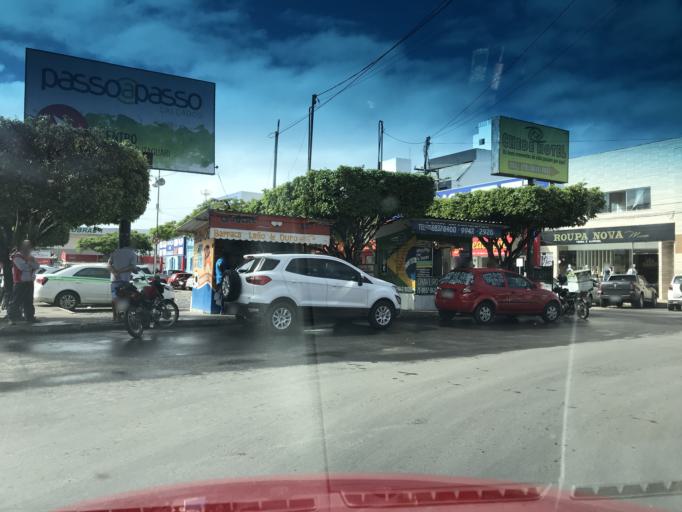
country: BR
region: Bahia
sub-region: Santo Antonio De Jesus
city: Santo Antonio de Jesus
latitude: -12.9662
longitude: -39.2642
